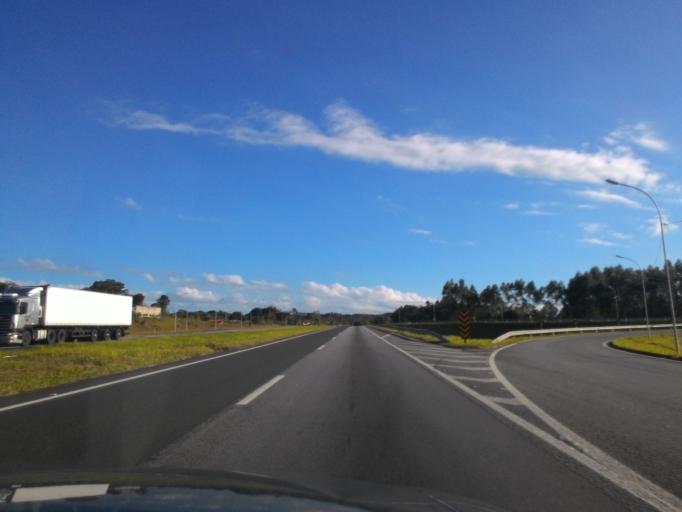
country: BR
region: Sao Paulo
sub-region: Pariquera-Acu
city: Pariquera Acu
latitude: -24.6444
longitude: -47.9189
